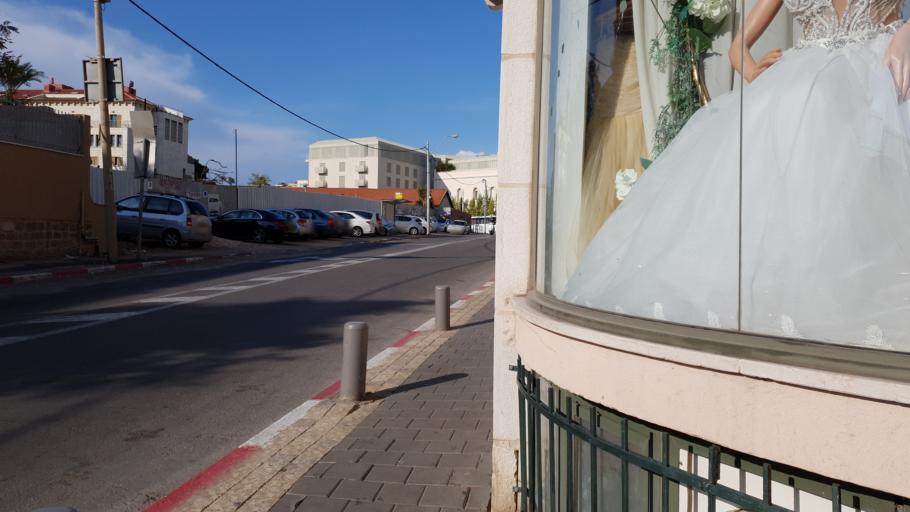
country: IL
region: Tel Aviv
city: Yafo
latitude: 32.0511
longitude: 34.7530
